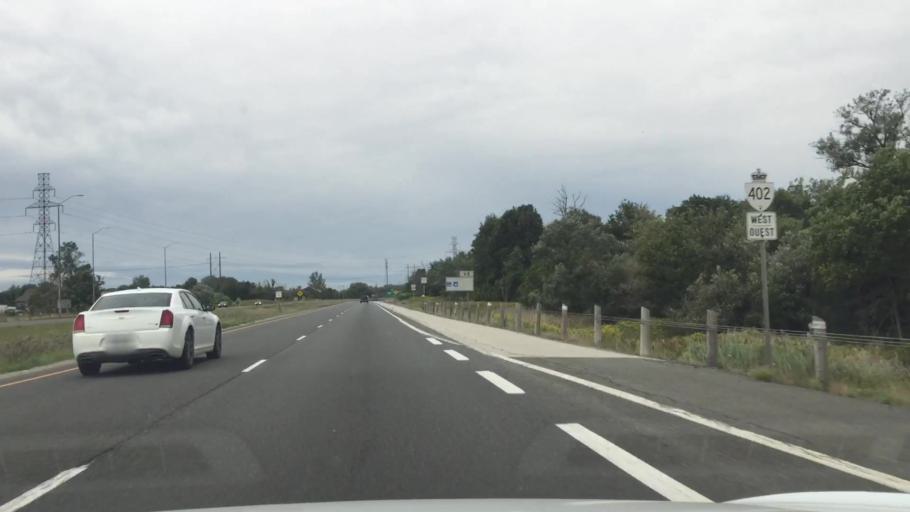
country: CA
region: Ontario
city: London
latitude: 42.8994
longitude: -81.2738
